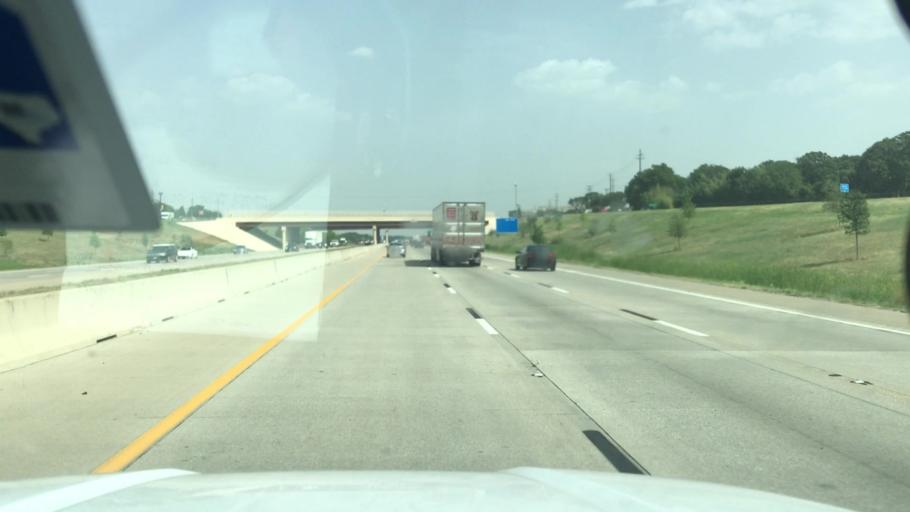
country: US
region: Texas
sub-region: Tarrant County
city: Southlake
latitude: 32.9537
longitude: -97.1368
